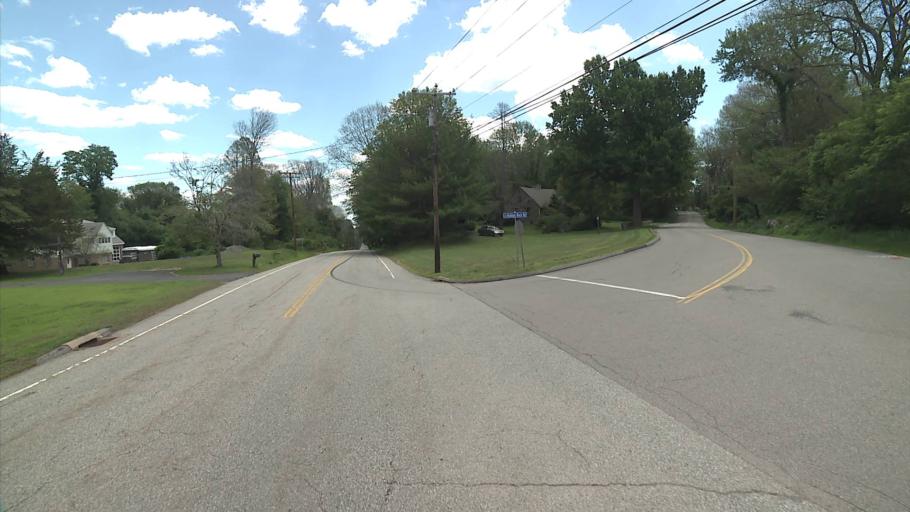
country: US
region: Connecticut
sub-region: Middlesex County
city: Higganum
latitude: 41.5233
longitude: -72.5224
